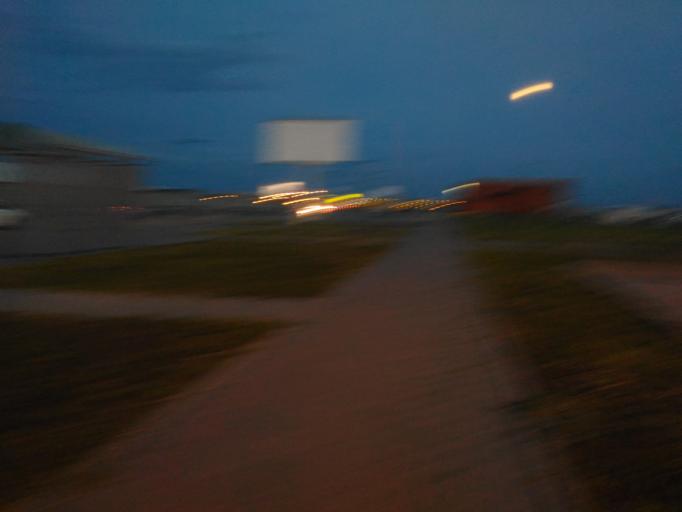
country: RU
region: Ulyanovsk
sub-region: Ulyanovskiy Rayon
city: Ulyanovsk
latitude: 54.2907
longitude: 48.2719
